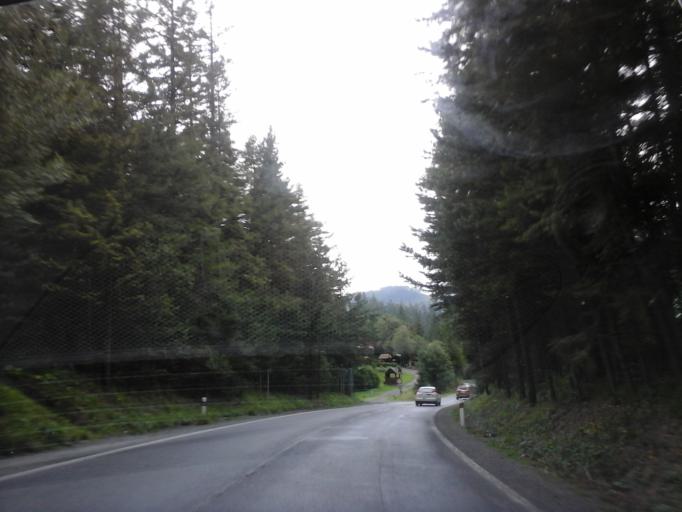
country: SK
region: Presovsky
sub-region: Okres Poprad
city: Zdiar
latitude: 49.2301
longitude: 20.3166
